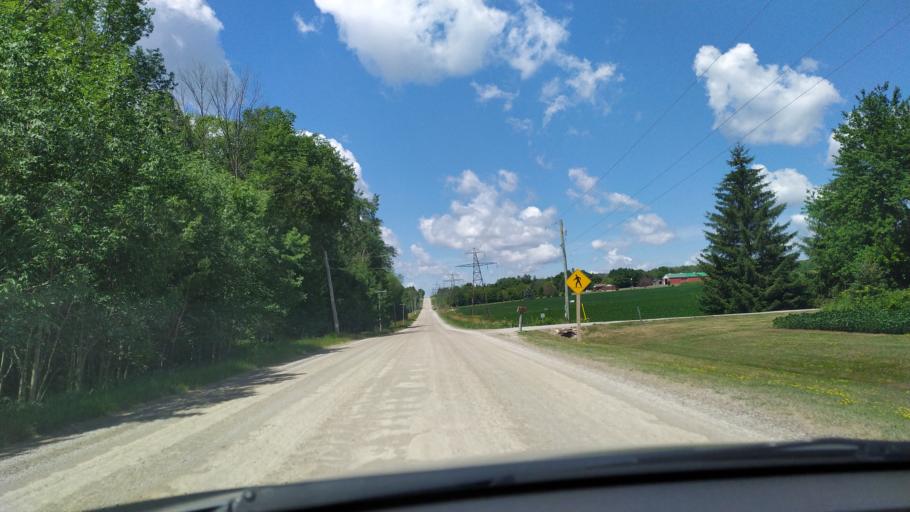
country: CA
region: Ontario
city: Stratford
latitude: 43.3876
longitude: -80.7940
